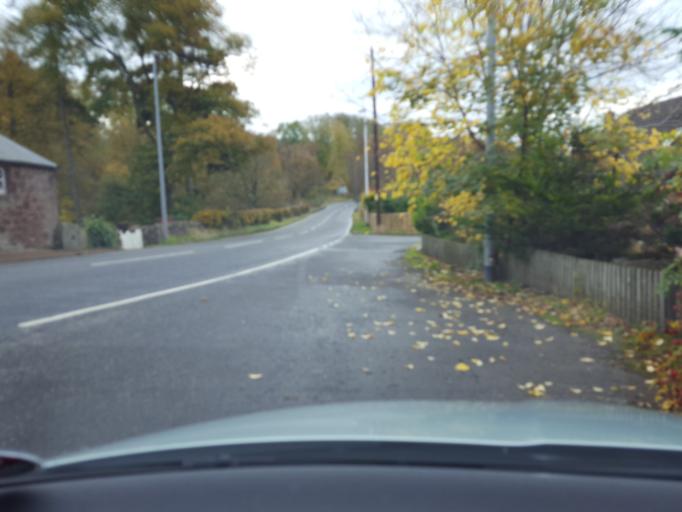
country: GB
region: Scotland
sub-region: The Scottish Borders
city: West Linton
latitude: 55.6932
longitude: -3.3825
